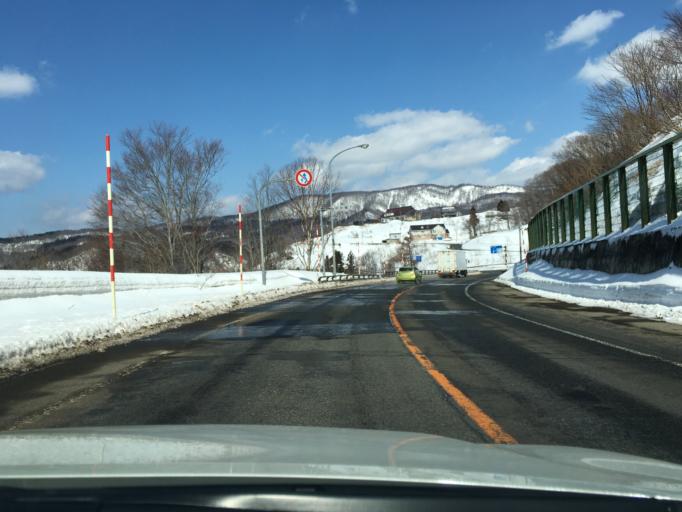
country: JP
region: Yamagata
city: Tsuruoka
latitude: 38.5687
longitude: 139.9367
